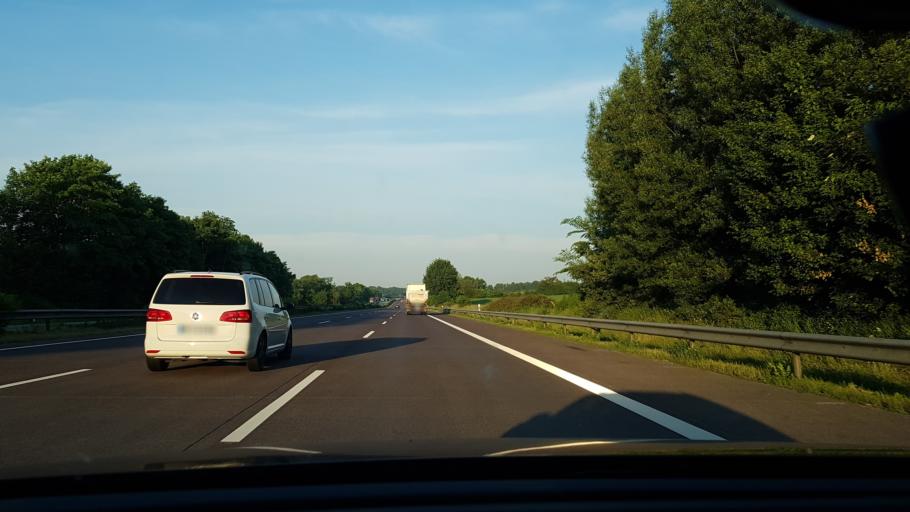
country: DE
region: Schleswig-Holstein
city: Wesenberg
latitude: 53.8371
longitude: 10.5654
